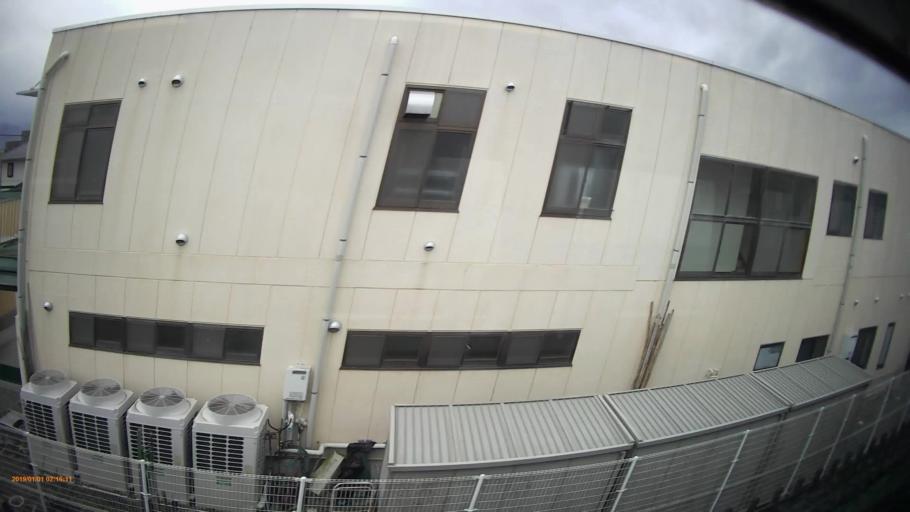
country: JP
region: Yamanashi
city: Kofu-shi
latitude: 35.6697
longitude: 138.5571
